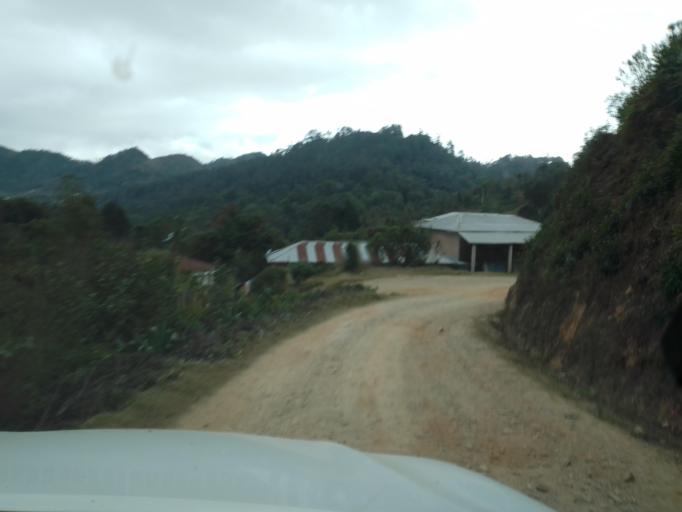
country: MX
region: Chiapas
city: Motozintla de Mendoza
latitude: 15.2166
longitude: -92.2325
